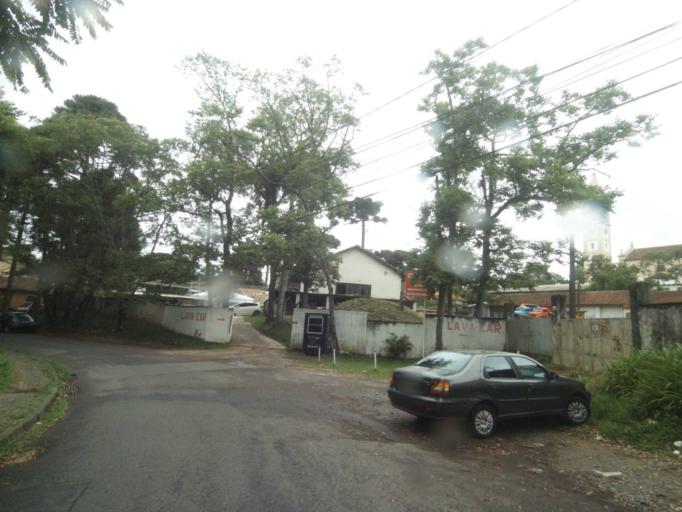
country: BR
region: Parana
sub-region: Curitiba
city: Curitiba
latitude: -25.4433
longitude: -49.3393
